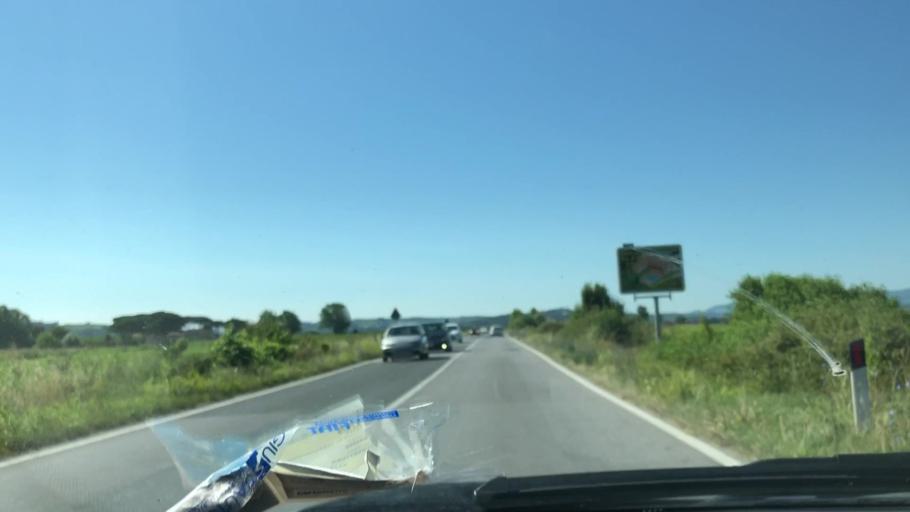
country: IT
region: Tuscany
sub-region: Province of Pisa
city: Forcoli
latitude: 43.5941
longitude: 10.6988
